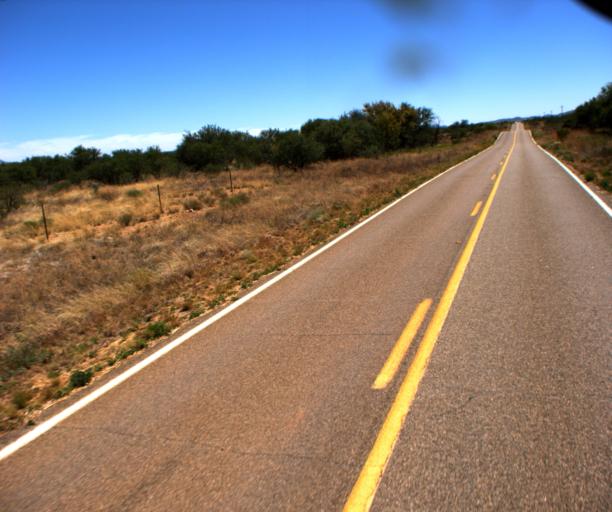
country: US
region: Arizona
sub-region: Pima County
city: Arivaca Junction
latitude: 31.6295
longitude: -111.5085
